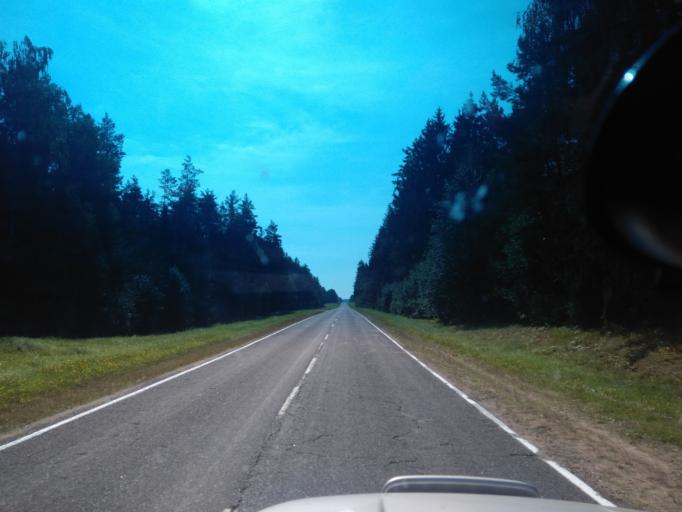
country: BY
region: Minsk
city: Uzda
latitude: 53.3309
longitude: 27.2306
